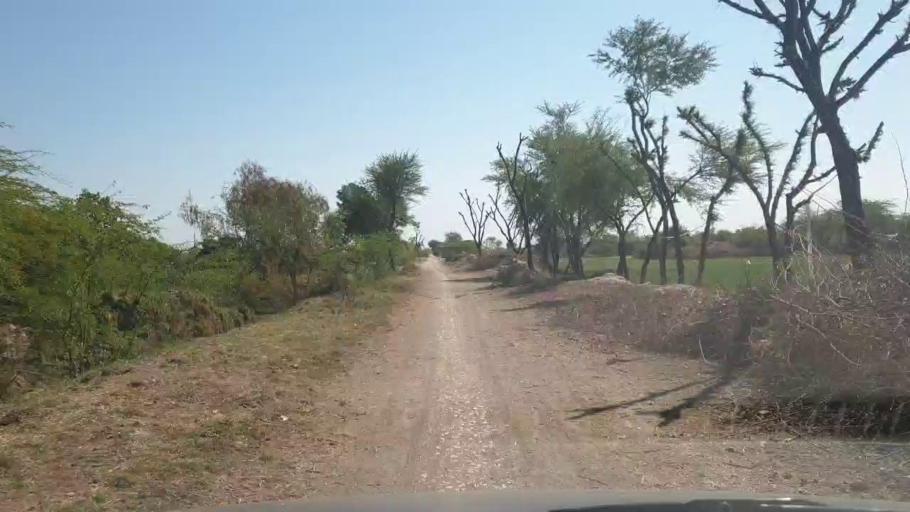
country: PK
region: Sindh
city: Umarkot
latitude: 25.3763
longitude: 69.6340
